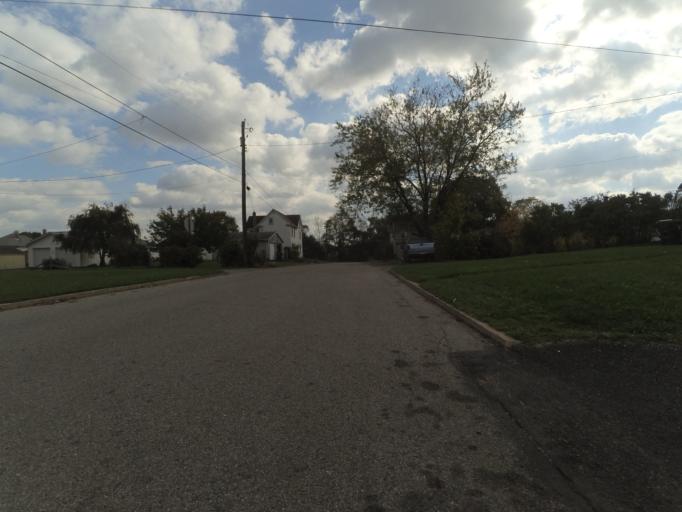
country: US
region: Pennsylvania
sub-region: Centre County
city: Bellefonte
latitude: 40.9108
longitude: -77.7863
